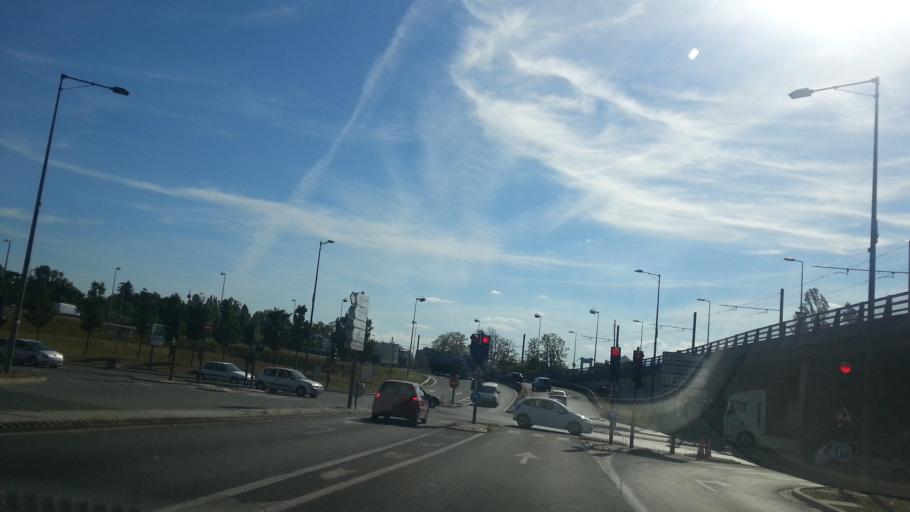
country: FR
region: Aquitaine
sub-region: Departement de la Gironde
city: Lormont
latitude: 44.8855
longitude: -0.5178
